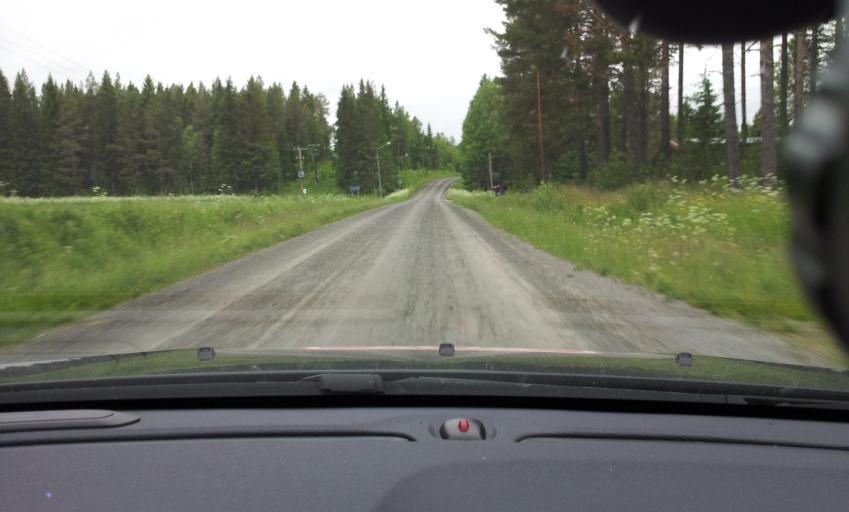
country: SE
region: Jaemtland
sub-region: Krokoms Kommun
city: Valla
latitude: 63.2586
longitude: 13.9309
